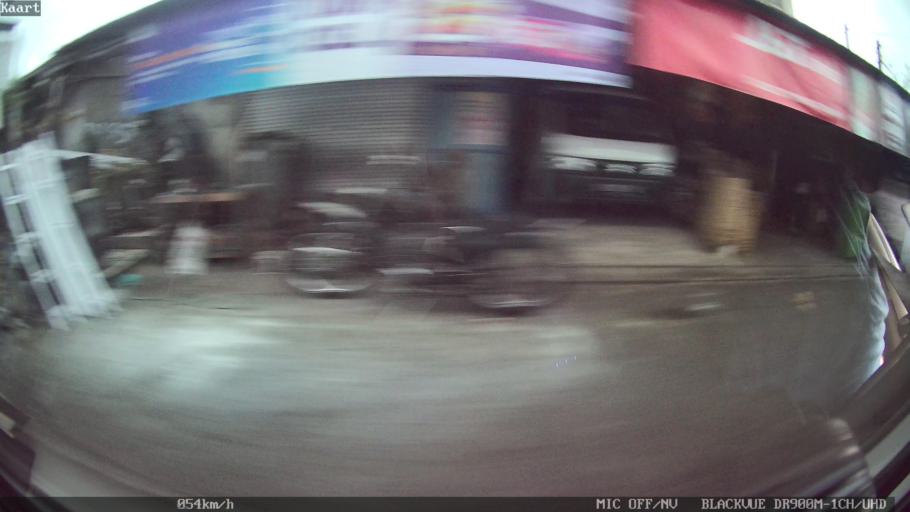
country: ID
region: Bali
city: Empalan
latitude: -8.4003
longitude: 115.1481
